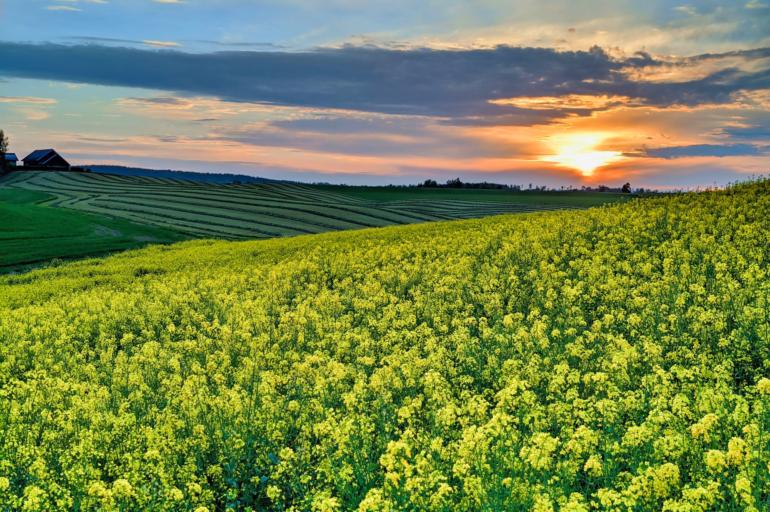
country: NO
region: Akershus
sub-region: Sorum
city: Sorumsand
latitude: 60.0231
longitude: 11.2128
